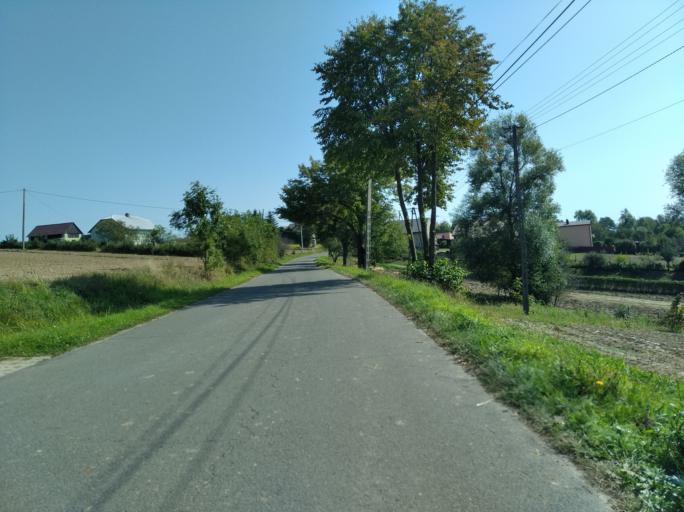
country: PL
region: Subcarpathian Voivodeship
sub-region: Powiat strzyzowski
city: Czudec
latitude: 49.9646
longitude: 21.8216
